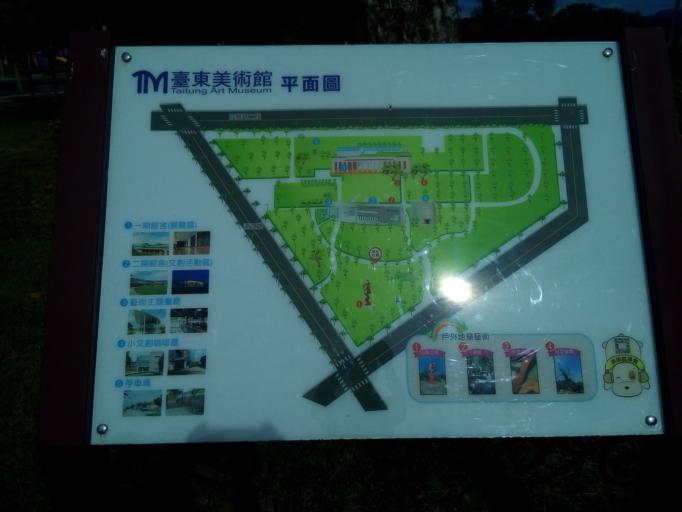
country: TW
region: Taiwan
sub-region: Taitung
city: Taitung
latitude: 22.7640
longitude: 121.1496
